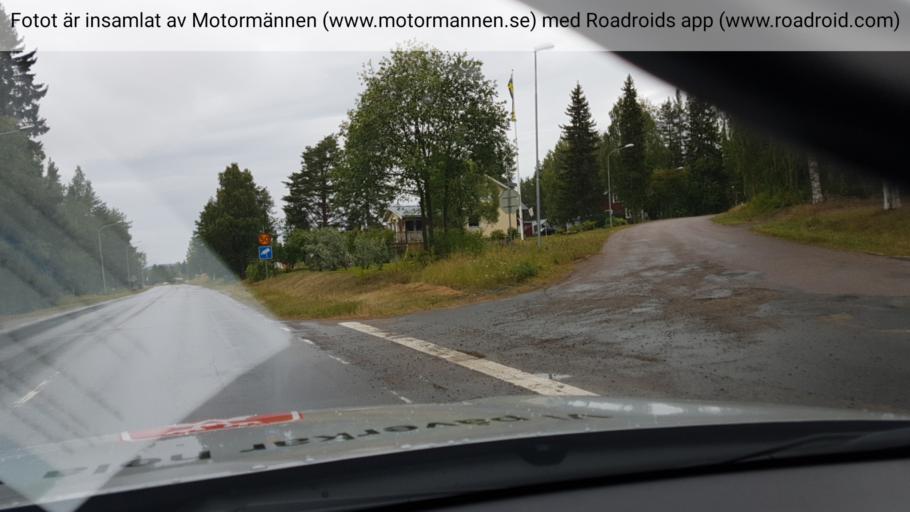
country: SE
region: Norrbotten
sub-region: Alvsbyns Kommun
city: AElvsbyn
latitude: 66.0949
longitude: 20.9441
